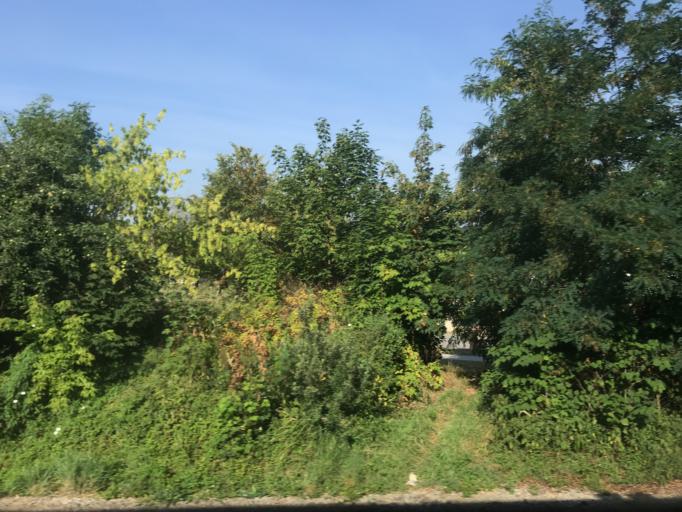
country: CZ
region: Jihocesky
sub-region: Okres Tabor
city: Sezimovo Usti
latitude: 49.4060
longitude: 14.6824
